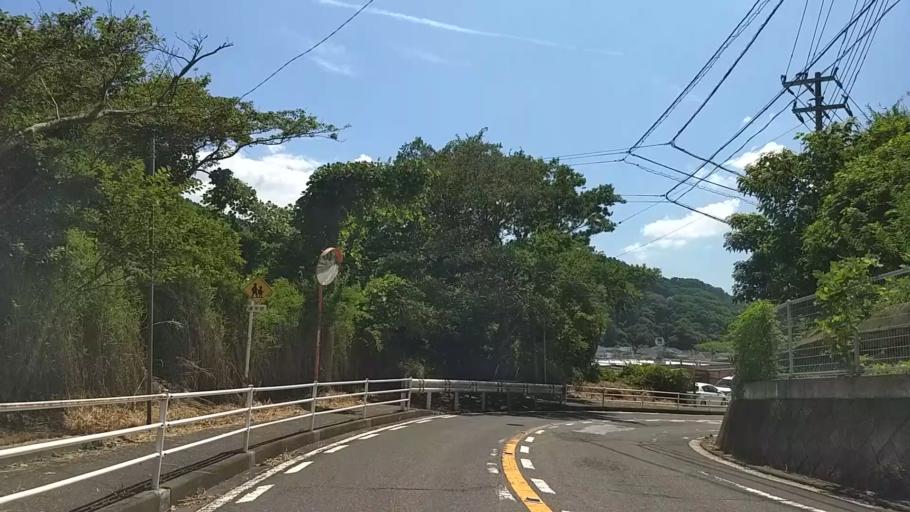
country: JP
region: Kanagawa
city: Zushi
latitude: 35.2860
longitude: 139.5913
